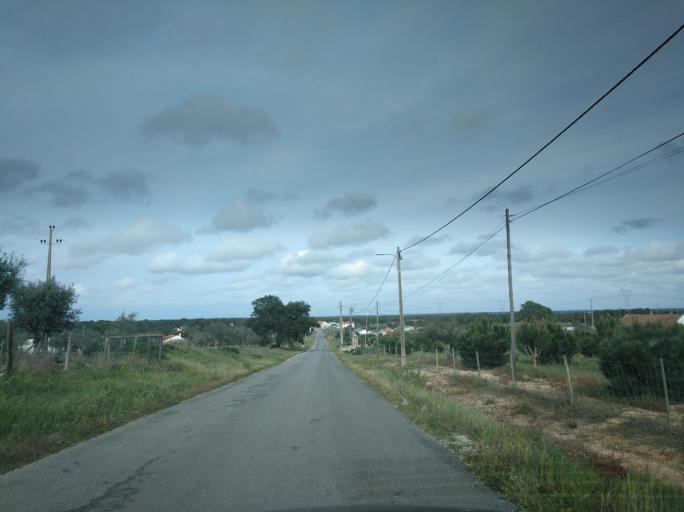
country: PT
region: Setubal
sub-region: Grandola
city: Grandola
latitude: 38.1947
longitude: -8.5502
